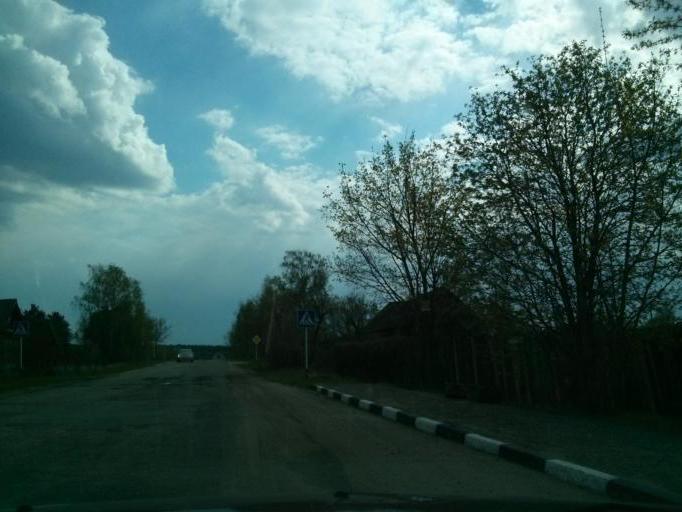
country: RU
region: Vladimir
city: Murom
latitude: 55.4623
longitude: 41.9786
